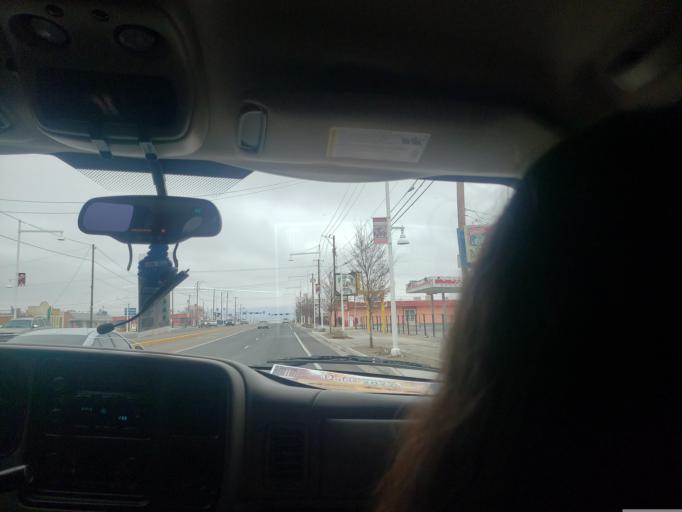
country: US
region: New Mexico
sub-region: Bernalillo County
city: Albuquerque
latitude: 35.0808
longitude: -106.7055
